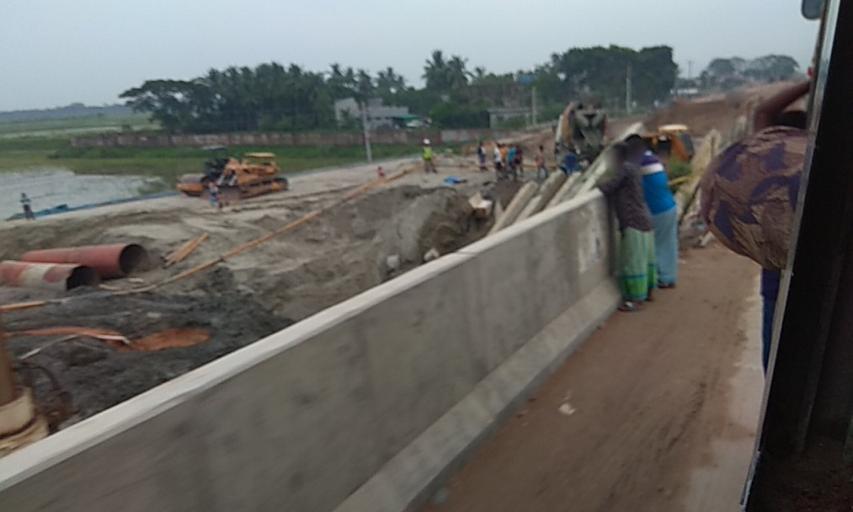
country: BD
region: Dhaka
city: Char Bhadrasan
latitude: 23.3884
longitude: 89.9878
